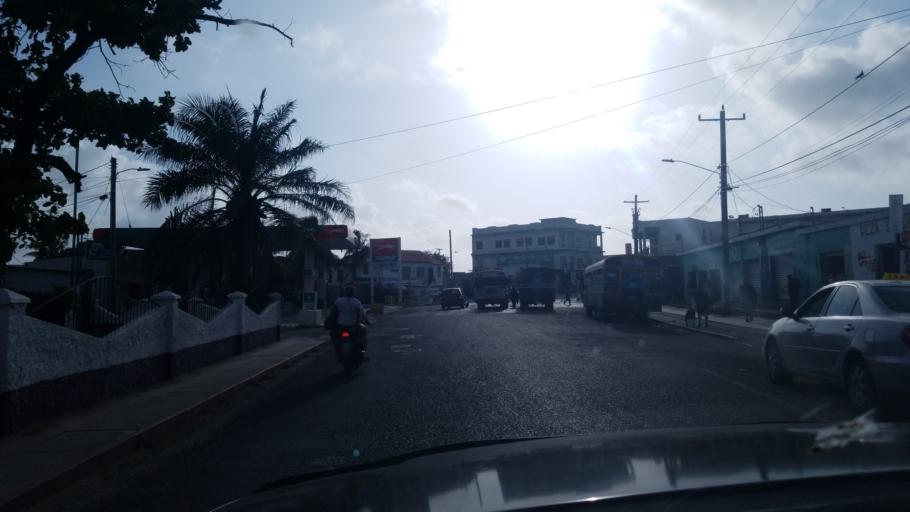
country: BZ
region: Belize
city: Belize City
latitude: 17.4949
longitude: -88.1936
